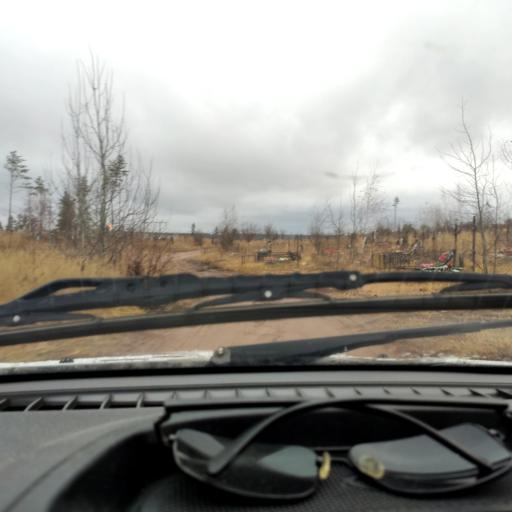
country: RU
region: Samara
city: Zhigulevsk
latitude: 53.5383
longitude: 49.5518
